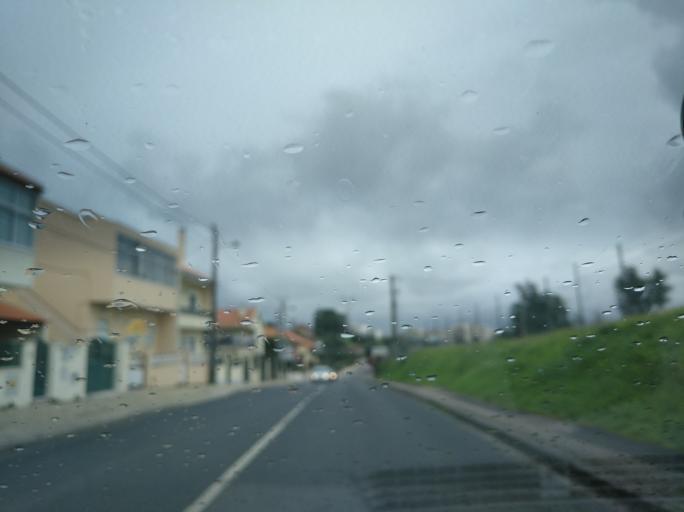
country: PT
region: Lisbon
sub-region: Odivelas
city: Famoes
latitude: 38.7910
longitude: -9.2016
